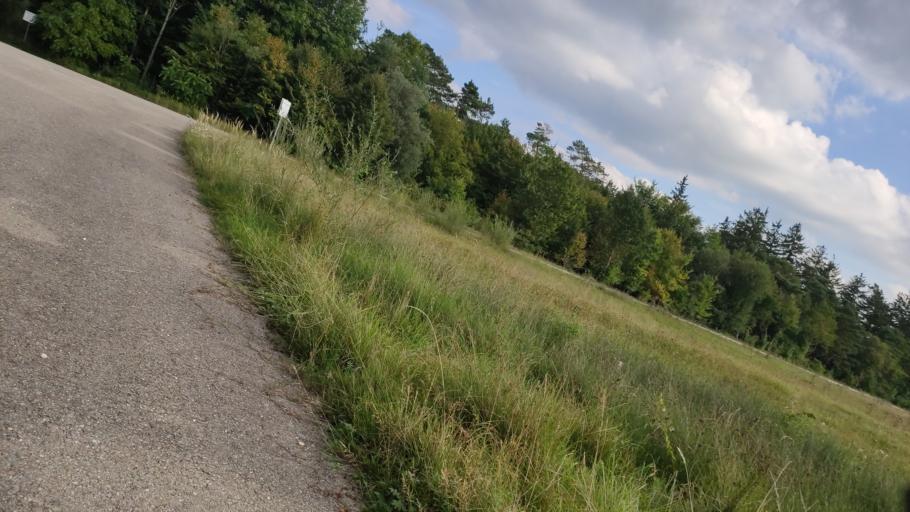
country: DE
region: Bavaria
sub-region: Upper Bavaria
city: Prittriching
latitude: 48.2155
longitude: 10.8945
